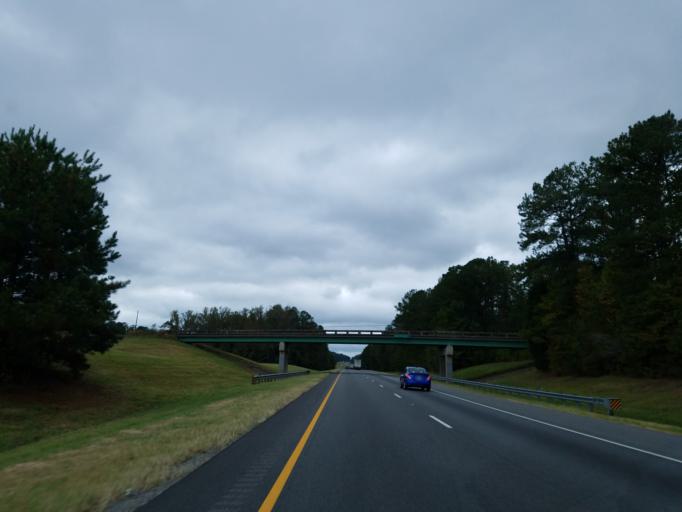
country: US
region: Alabama
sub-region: Hale County
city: Moundville
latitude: 33.0058
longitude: -87.7643
